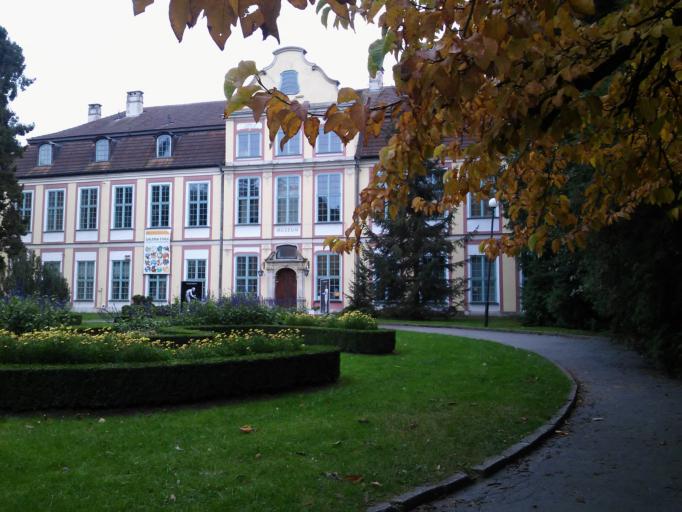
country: PL
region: Pomeranian Voivodeship
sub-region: Sopot
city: Sopot
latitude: 54.4113
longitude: 18.5596
